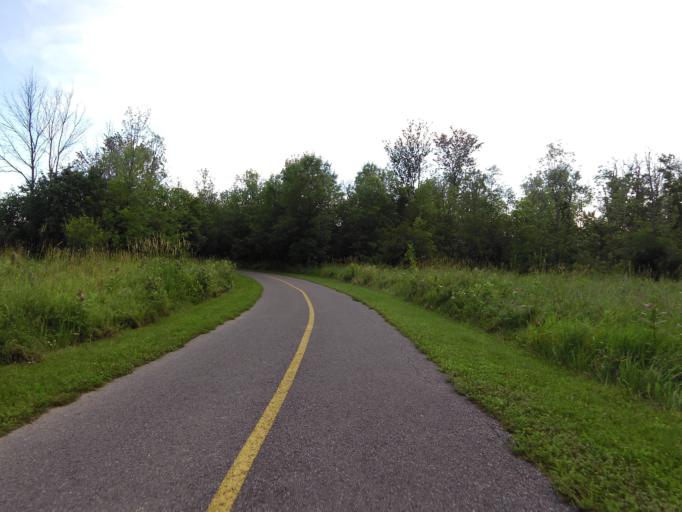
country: CA
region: Ontario
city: Bells Corners
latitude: 45.3369
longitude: -75.8861
